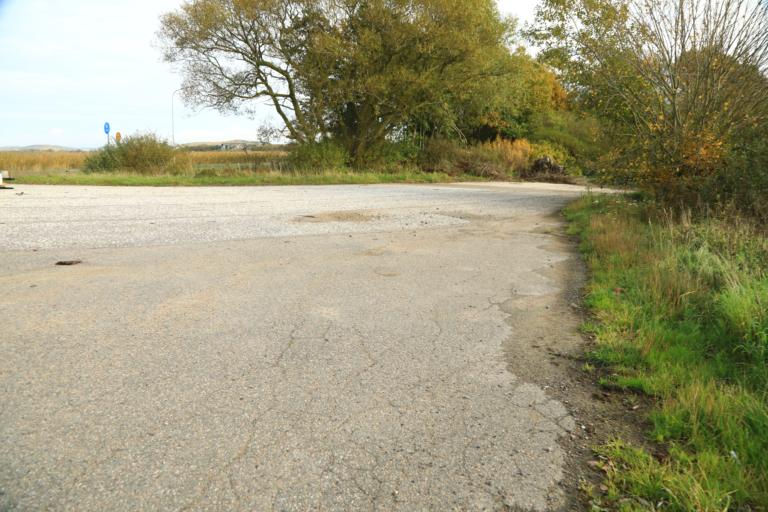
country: SE
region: Halland
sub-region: Varbergs Kommun
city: Varberg
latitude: 57.1219
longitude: 12.2440
